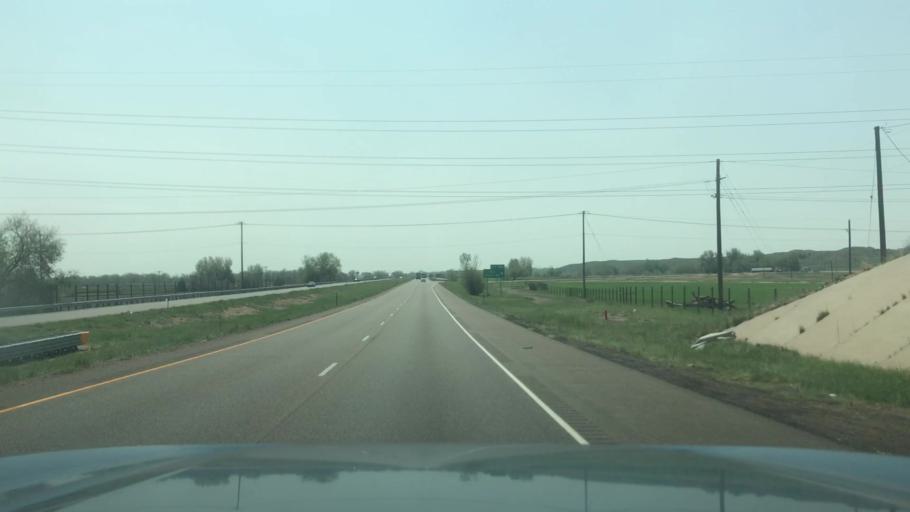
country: US
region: Colorado
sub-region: El Paso County
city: Fountain
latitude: 38.6334
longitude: -104.6919
